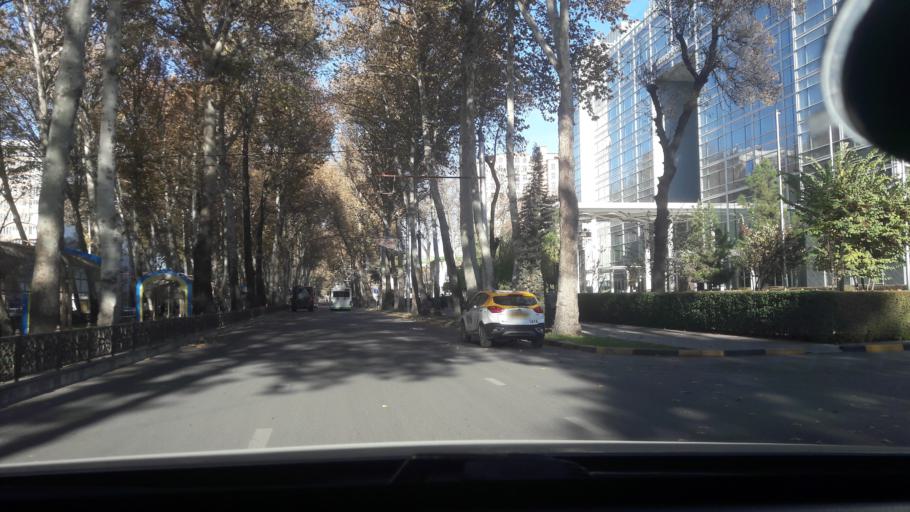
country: TJ
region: Dushanbe
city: Dushanbe
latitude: 38.5632
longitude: 68.7983
